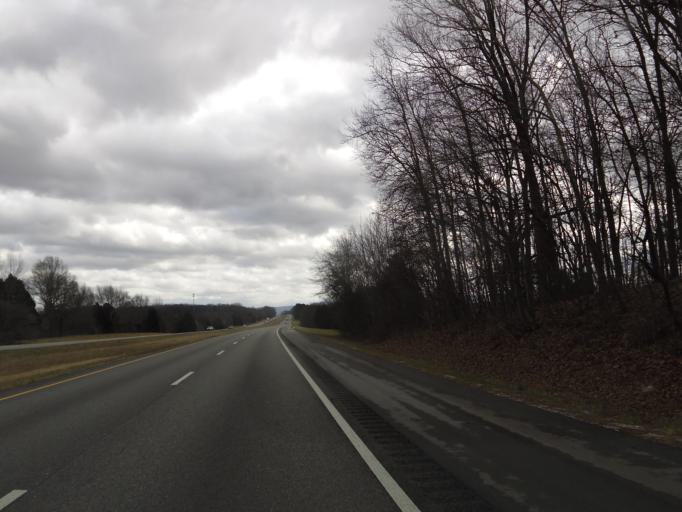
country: US
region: Tennessee
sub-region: Franklin County
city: Sewanee
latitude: 35.3475
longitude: -85.9462
